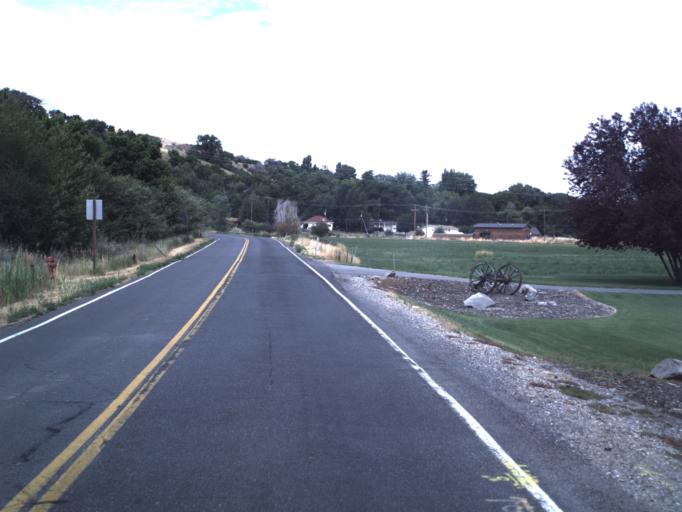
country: US
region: Utah
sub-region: Weber County
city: Riverdale
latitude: 41.1570
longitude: -111.9990
